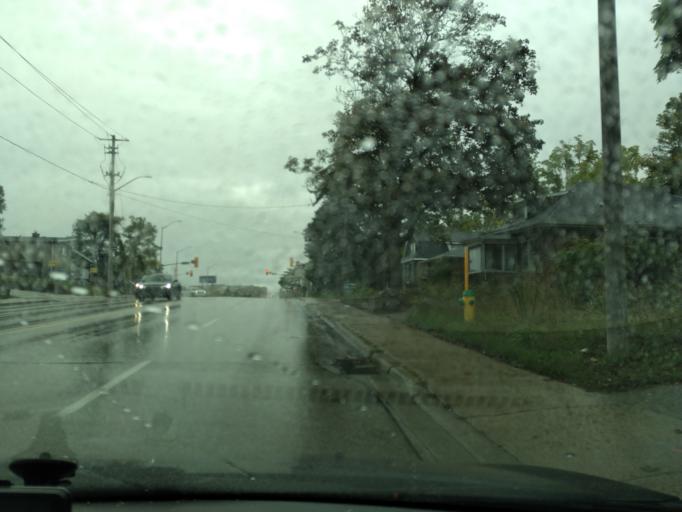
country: CA
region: Ontario
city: Barrie
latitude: 44.3979
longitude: -79.6974
